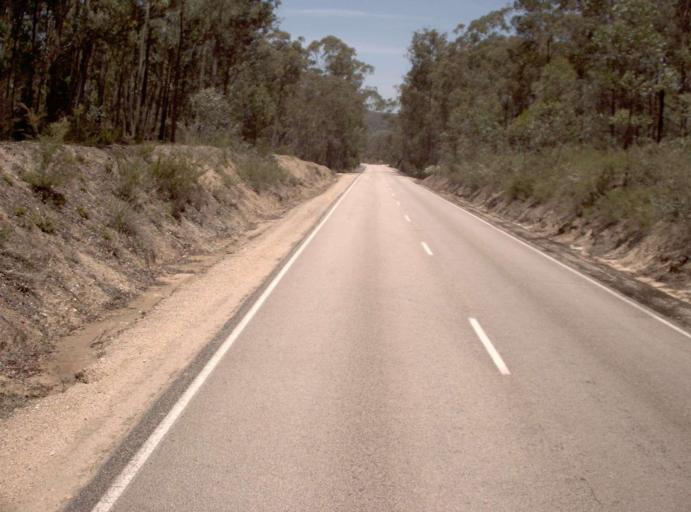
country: AU
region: Victoria
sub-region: East Gippsland
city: Lakes Entrance
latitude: -37.6555
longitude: 147.8799
